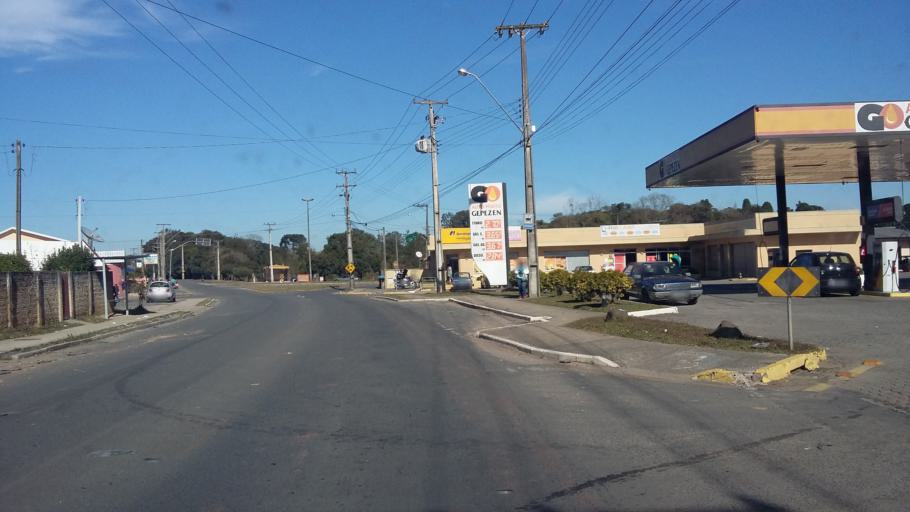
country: BR
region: Parana
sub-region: Campo Largo
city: Campo Largo
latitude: -25.4676
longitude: -49.5660
